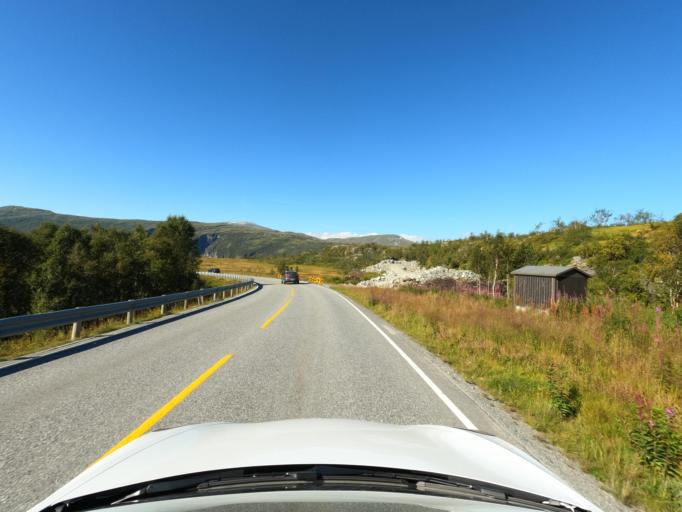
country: NO
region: Hordaland
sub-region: Eidfjord
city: Eidfjord
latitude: 60.4124
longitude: 7.2654
